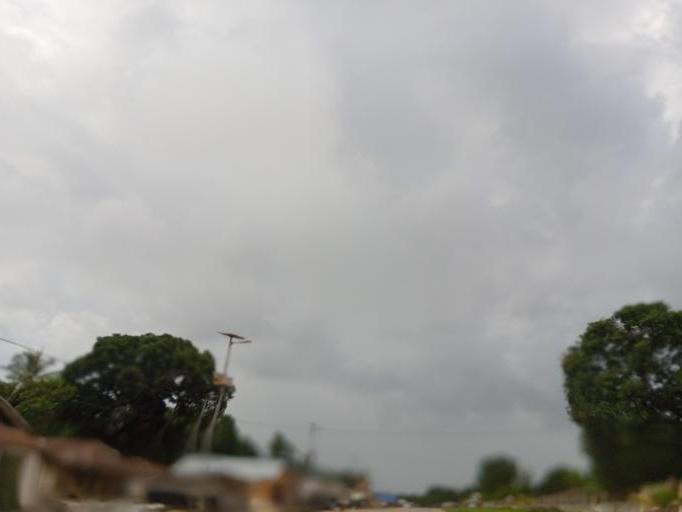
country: SL
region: Northern Province
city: Sawkta
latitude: 8.6273
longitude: -13.2056
